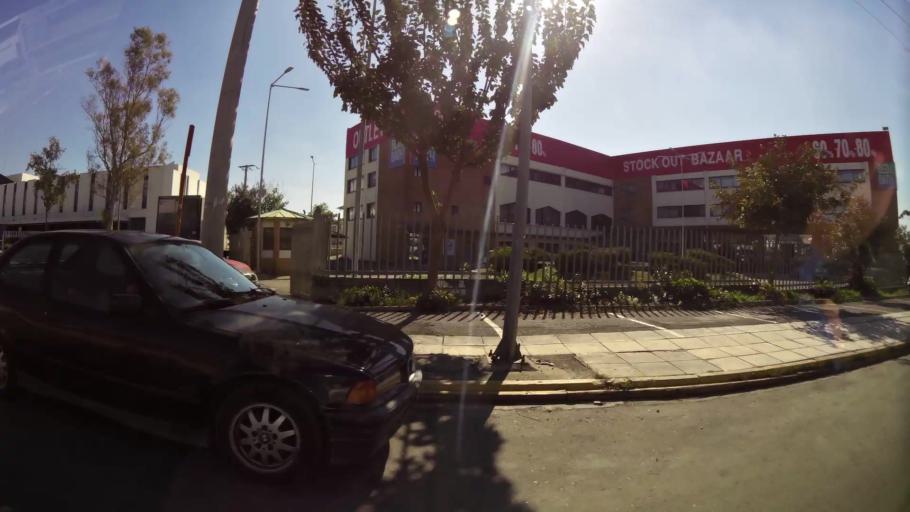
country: GR
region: Attica
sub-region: Nomarchia Athinas
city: Metamorfosi
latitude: 38.0719
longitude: 23.7688
